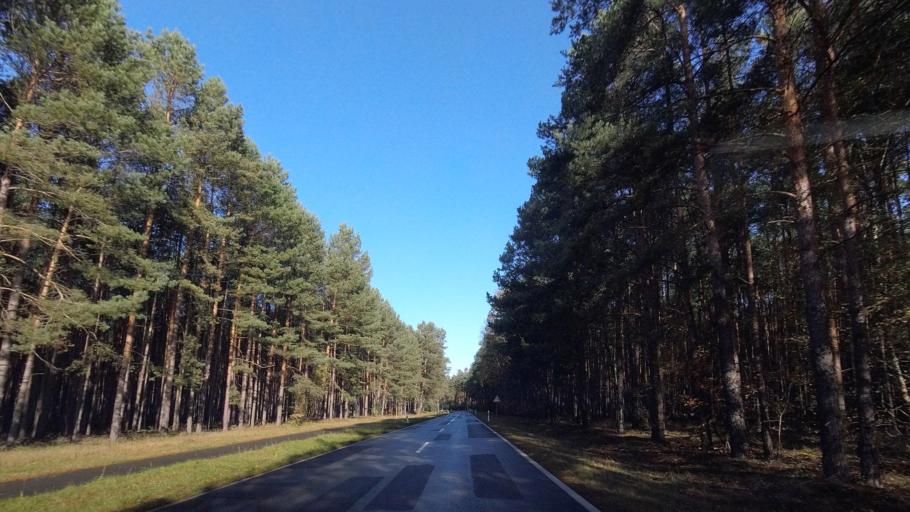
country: DE
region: Brandenburg
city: Borkwalde
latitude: 52.2437
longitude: 12.8508
